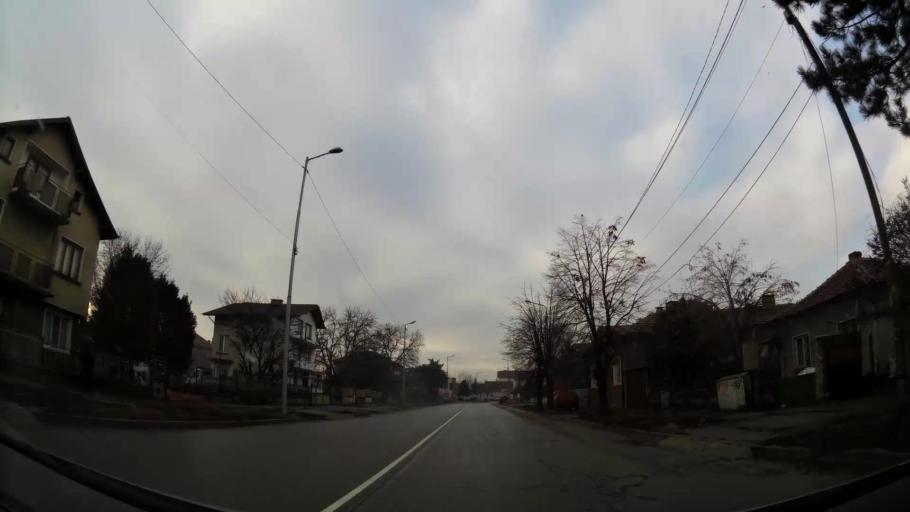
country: BG
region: Sofia-Capital
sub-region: Stolichna Obshtina
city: Sofia
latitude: 42.7473
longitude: 23.3504
